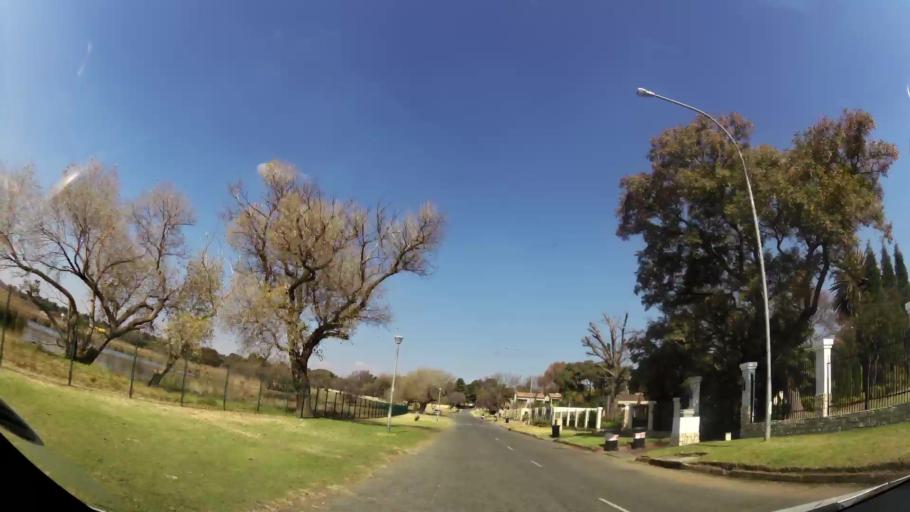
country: ZA
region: Gauteng
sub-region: Ekurhuleni Metropolitan Municipality
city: Benoni
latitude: -26.1939
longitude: 28.2905
